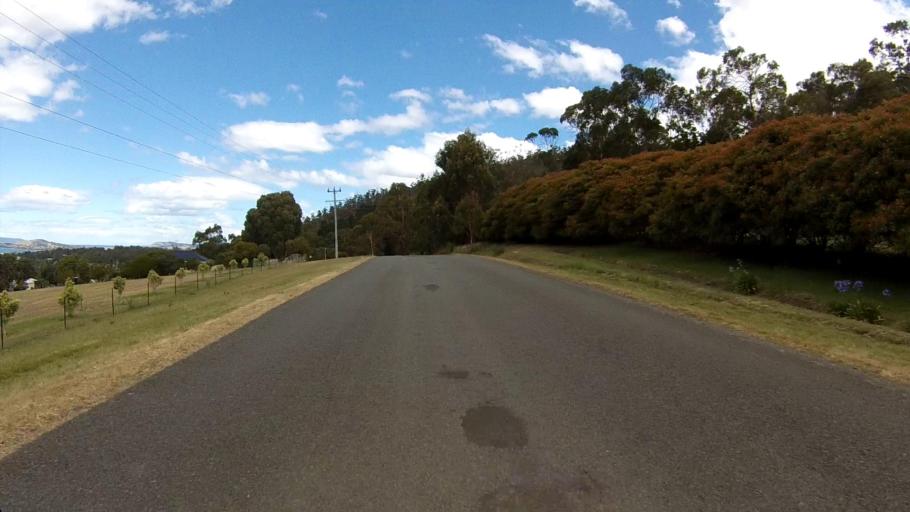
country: AU
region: Tasmania
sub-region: Clarence
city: Acton Park
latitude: -42.8633
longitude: 147.4698
